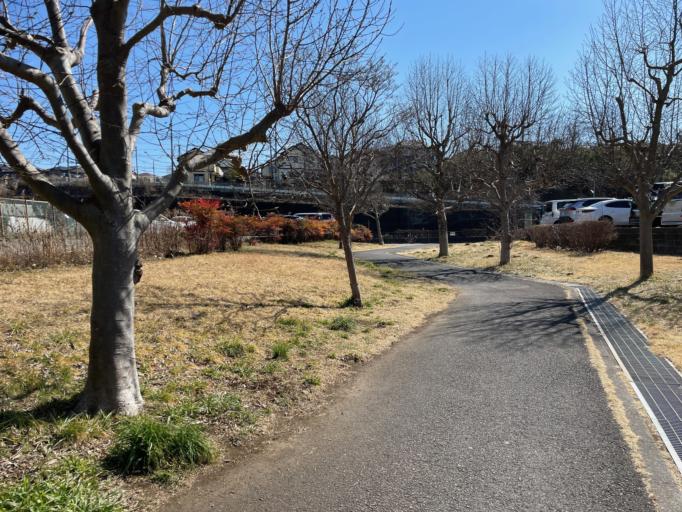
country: JP
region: Tokyo
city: Hino
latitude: 35.6842
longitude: 139.3757
